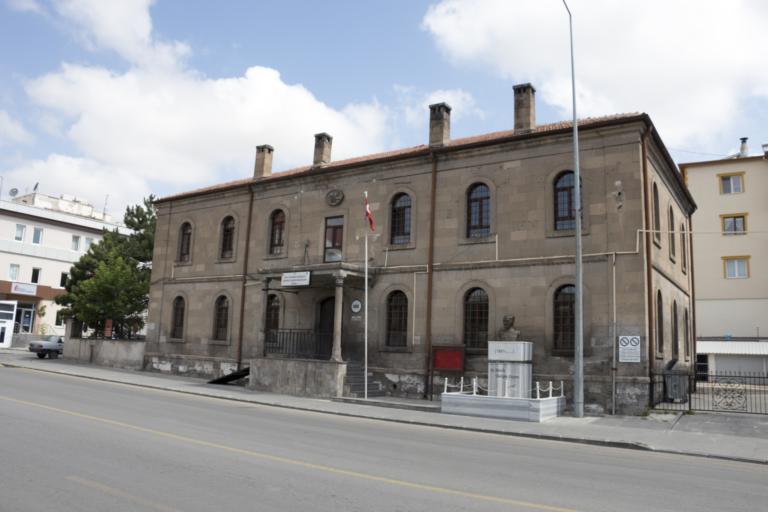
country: TR
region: Kayseri
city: Develi
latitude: 38.3893
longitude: 35.4904
